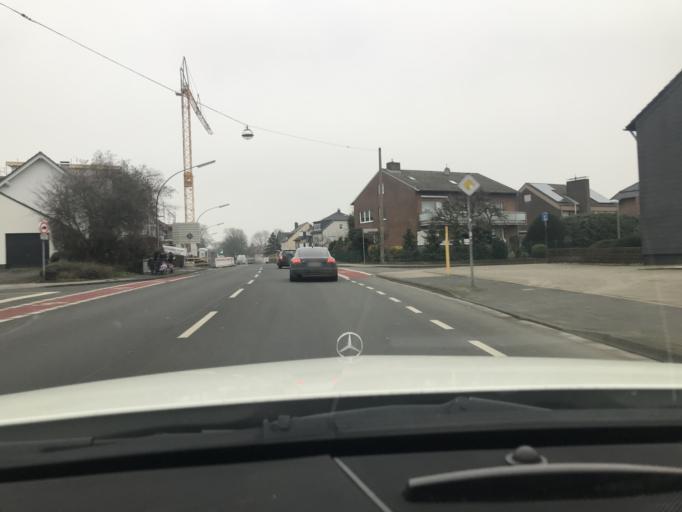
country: DE
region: North Rhine-Westphalia
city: Waltrop
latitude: 51.6147
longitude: 7.4046
